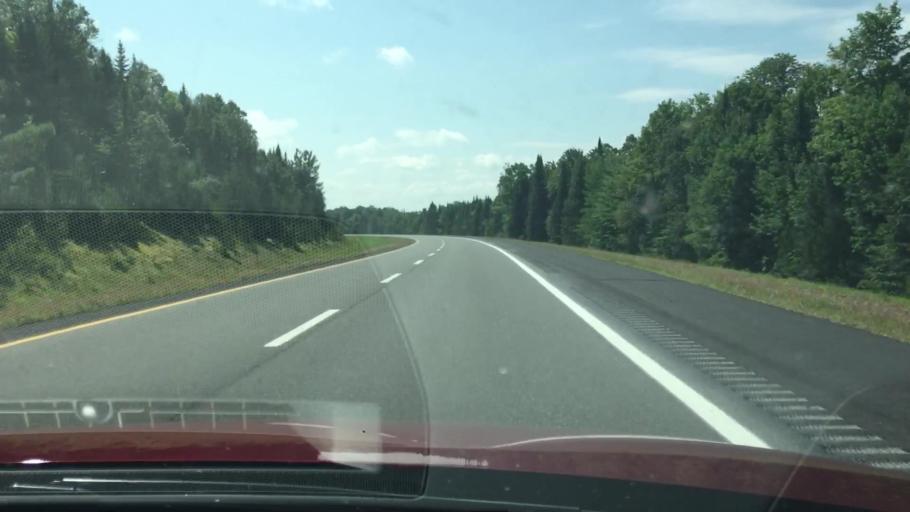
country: US
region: Maine
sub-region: Penobscot County
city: Patten
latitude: 45.9328
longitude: -68.3588
